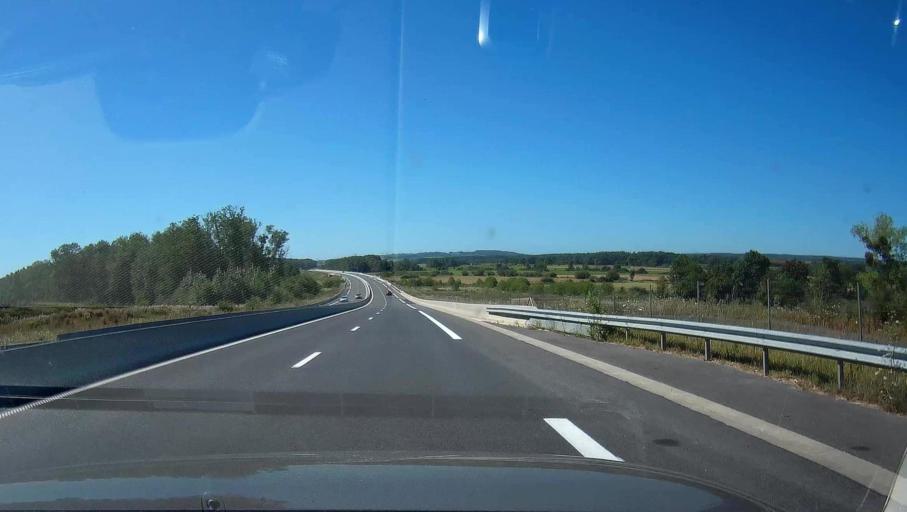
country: FR
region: Champagne-Ardenne
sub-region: Departement des Ardennes
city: Tournes
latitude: 49.7847
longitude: 4.5972
